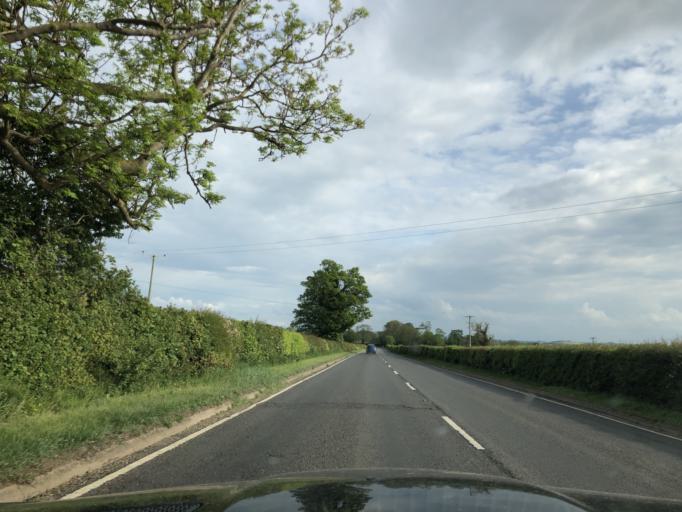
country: GB
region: England
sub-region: Warwickshire
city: Shipston on Stour
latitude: 52.1182
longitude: -1.6200
